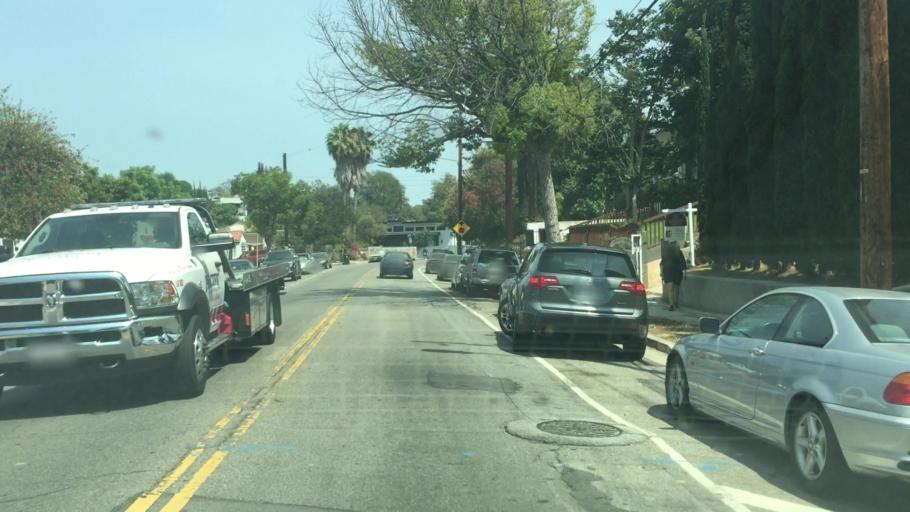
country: US
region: California
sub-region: Los Angeles County
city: Glendale
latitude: 34.1161
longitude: -118.2130
